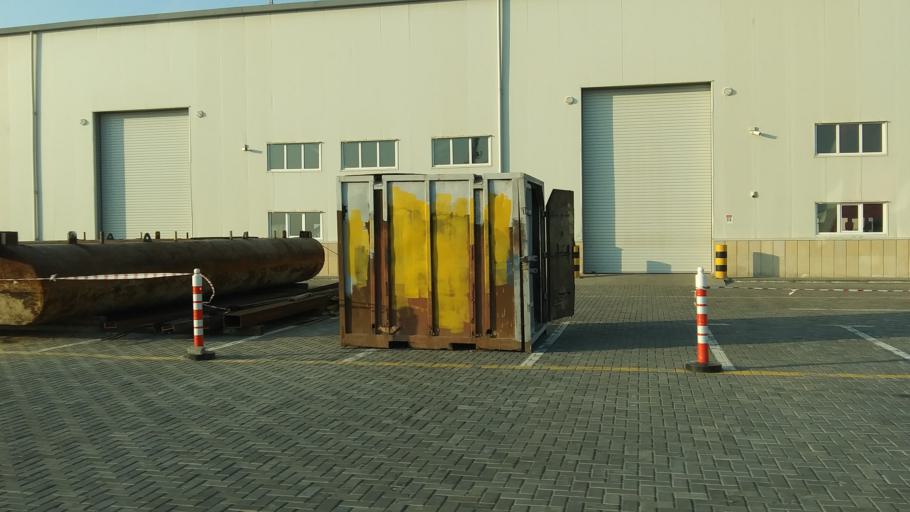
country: AZ
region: Baki
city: Qobustan
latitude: 39.9786
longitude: 49.4491
